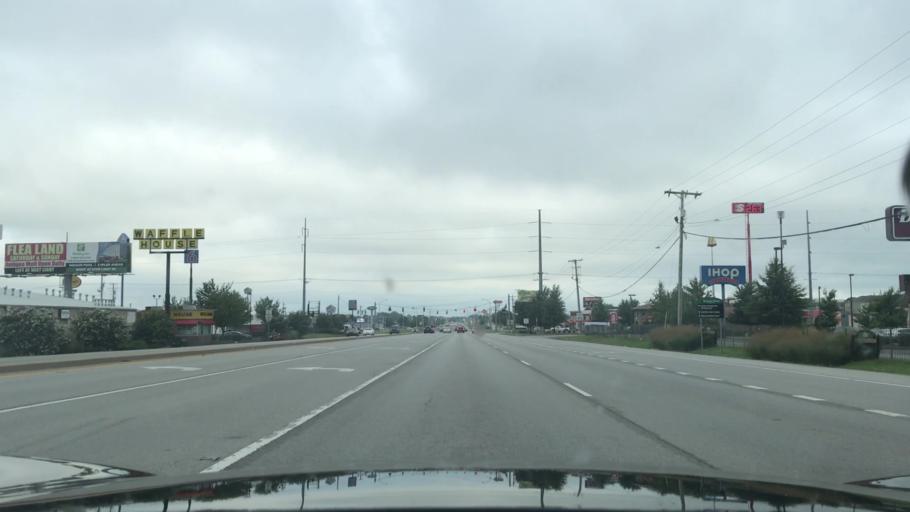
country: US
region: Kentucky
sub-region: Warren County
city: Bowling Green
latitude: 36.9381
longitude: -86.4198
